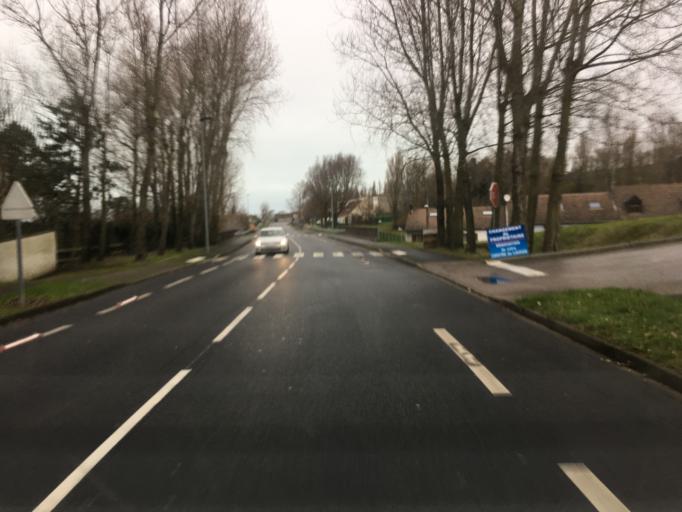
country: FR
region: Nord-Pas-de-Calais
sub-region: Departement du Pas-de-Calais
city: Le Portel
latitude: 50.6991
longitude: 1.5801
